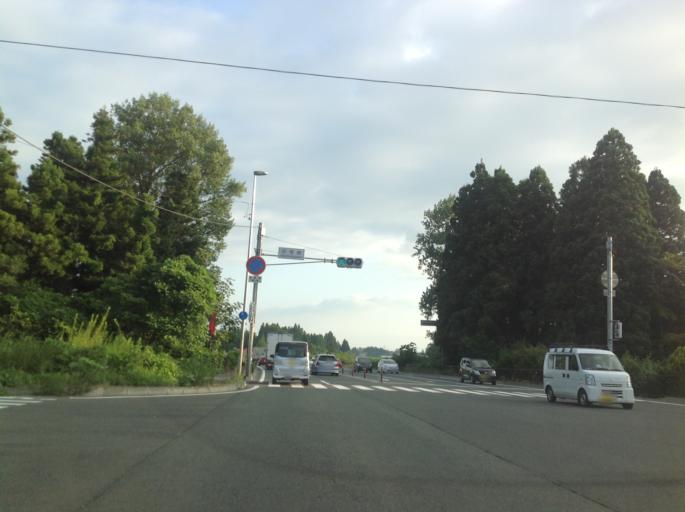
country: JP
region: Iwate
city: Hanamaki
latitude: 39.4793
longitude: 141.1396
